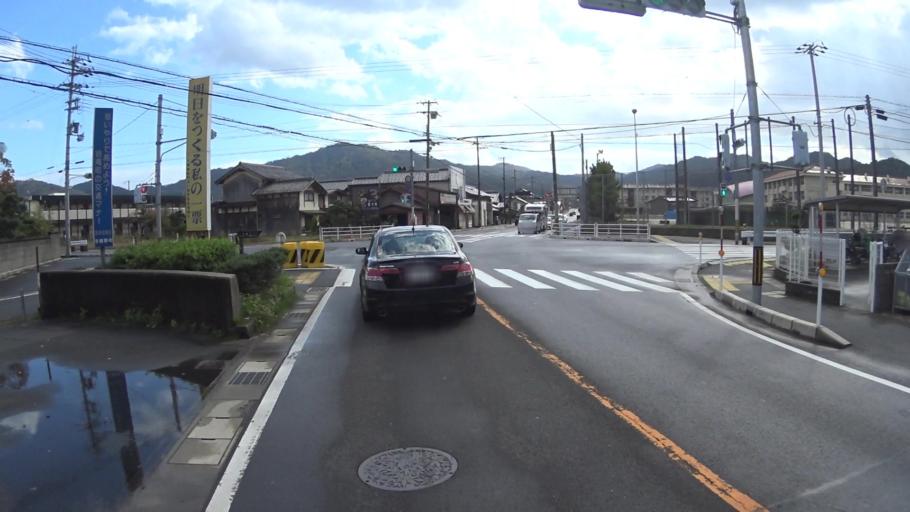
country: JP
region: Kyoto
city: Miyazu
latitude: 35.5630
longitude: 135.1530
